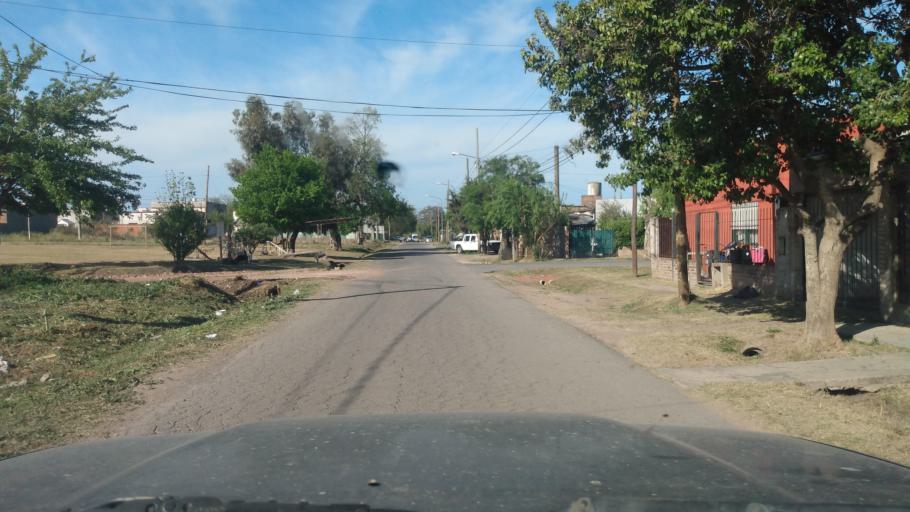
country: AR
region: Buenos Aires
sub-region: Partido de Lujan
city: Lujan
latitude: -34.5681
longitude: -59.1379
